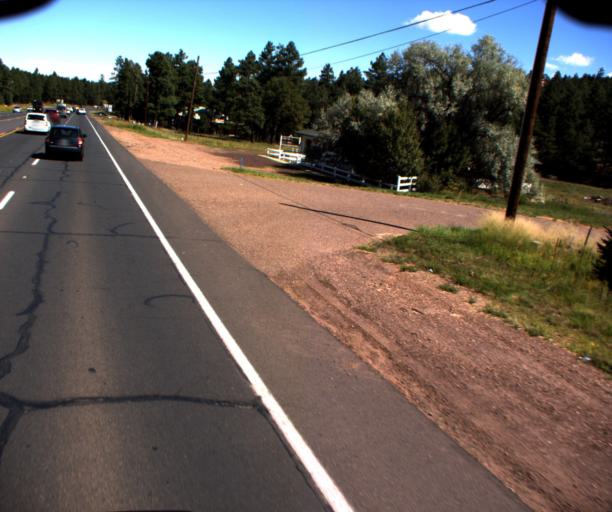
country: US
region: Arizona
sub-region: Navajo County
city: Show Low
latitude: 34.2189
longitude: -110.0289
